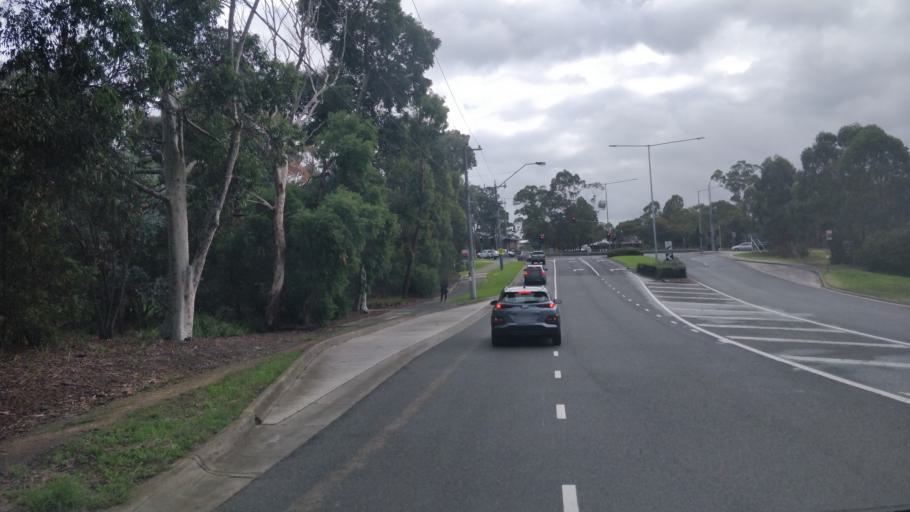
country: AU
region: Victoria
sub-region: Manningham
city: Donvale
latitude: -37.7667
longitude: 145.1826
